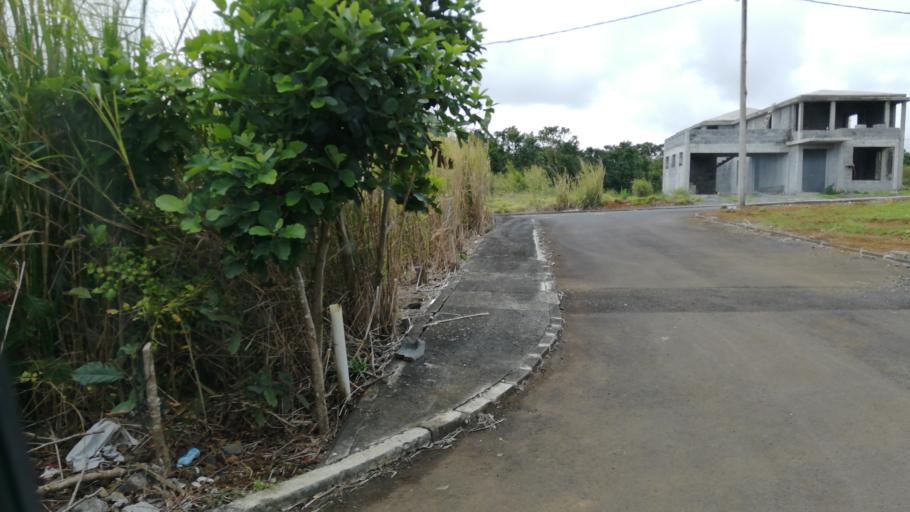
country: MU
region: Moka
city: La Dagotiere
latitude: -20.2677
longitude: 57.5367
